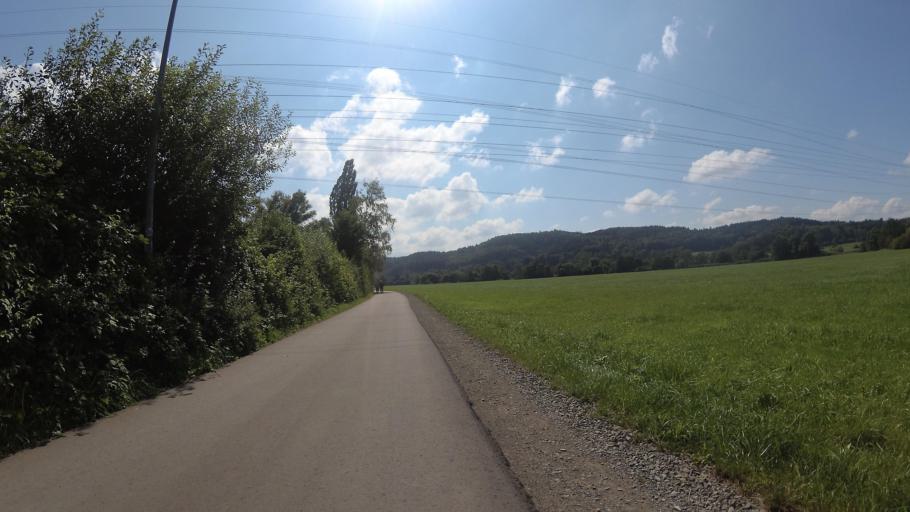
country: DE
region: Saarland
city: Homburg
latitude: 49.3006
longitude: 7.3056
